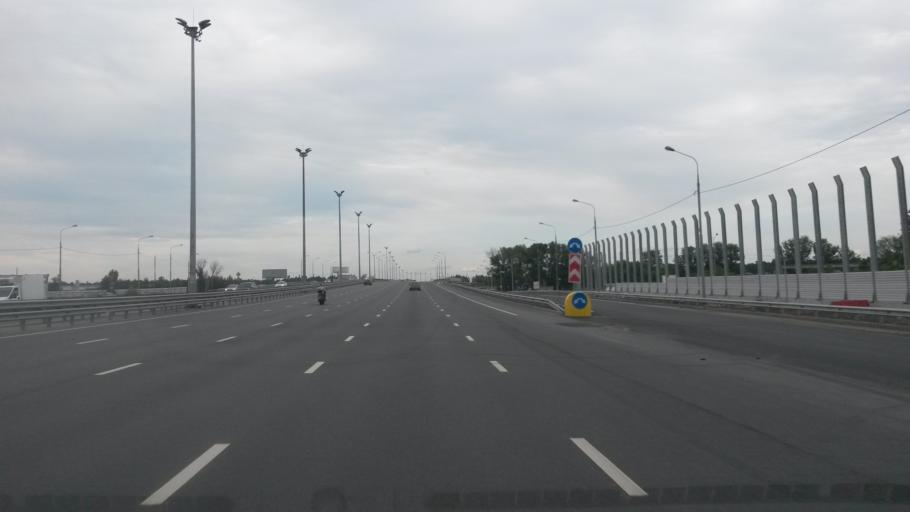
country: RU
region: Moskovskaya
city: Mamontovka
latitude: 55.9614
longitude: 37.8359
